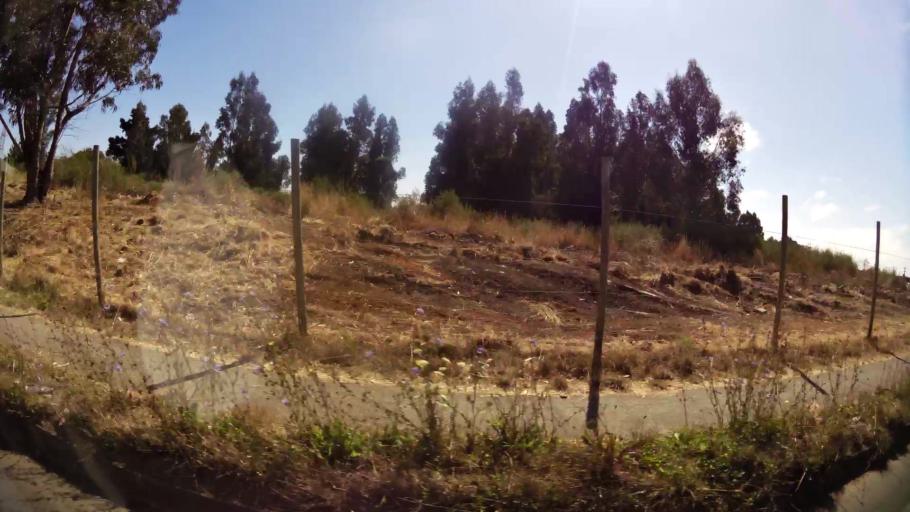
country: CL
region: Biobio
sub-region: Provincia de Concepcion
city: Concepcion
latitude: -36.7863
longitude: -73.0547
